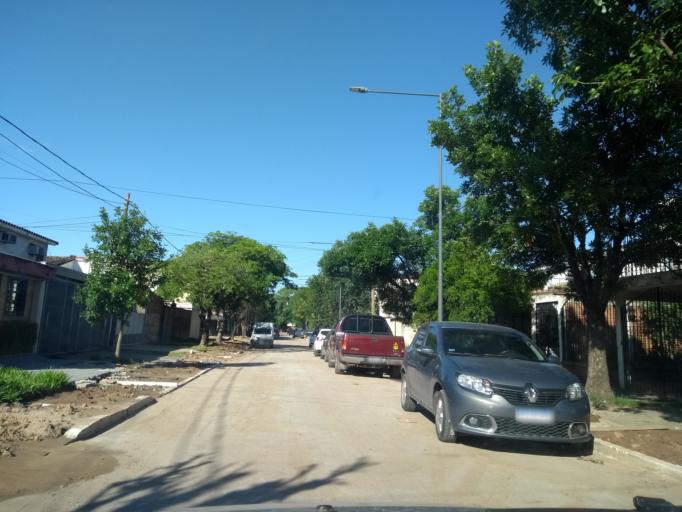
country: AR
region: Chaco
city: Resistencia
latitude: -27.4753
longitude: -58.9818
